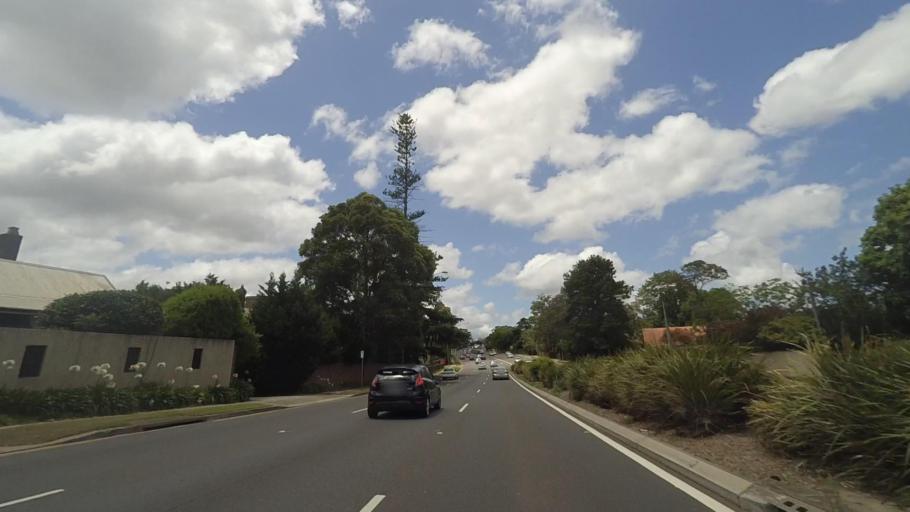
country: AU
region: New South Wales
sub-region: Ku-ring-gai
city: Normanhurst
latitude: -33.7237
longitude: 151.0993
